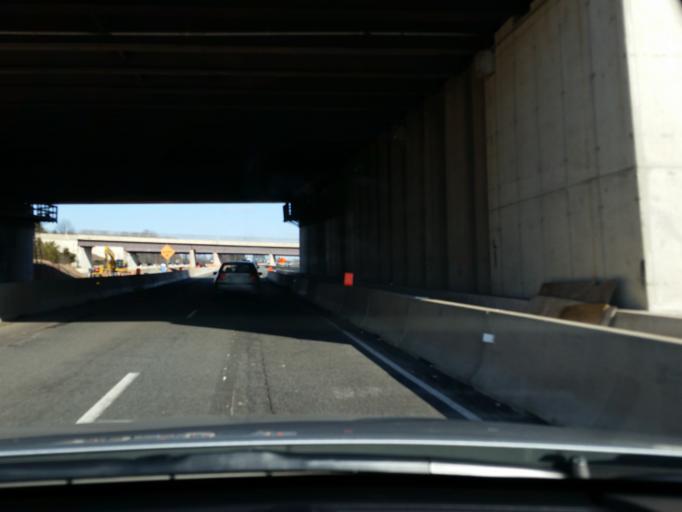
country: US
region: Virginia
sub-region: Fairfax County
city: Floris
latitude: 38.9624
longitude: -77.4281
